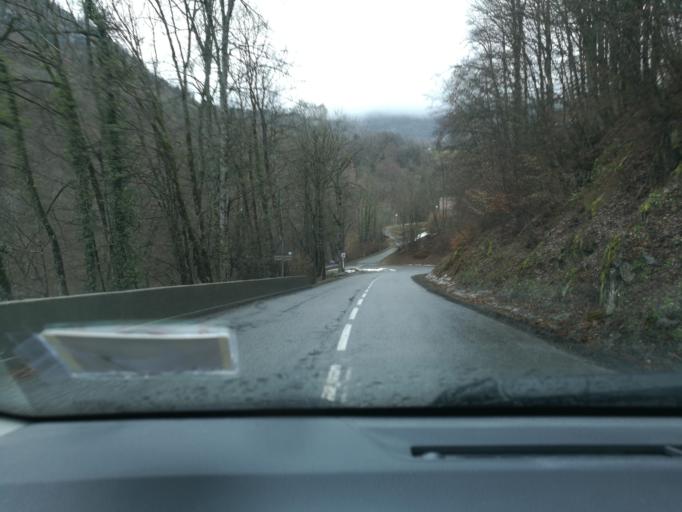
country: FR
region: Rhone-Alpes
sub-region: Departement de la Haute-Savoie
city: Araches-la-Frasse
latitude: 46.0473
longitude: 6.6152
